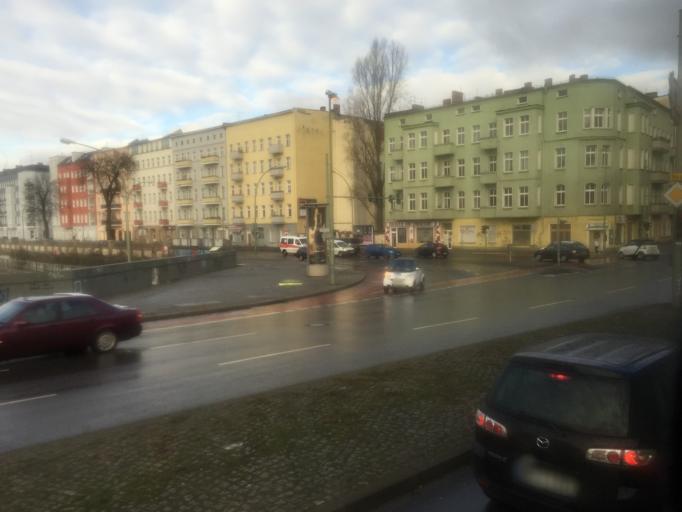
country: DE
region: Berlin
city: Treptow Bezirk
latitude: 52.4970
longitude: 13.4644
